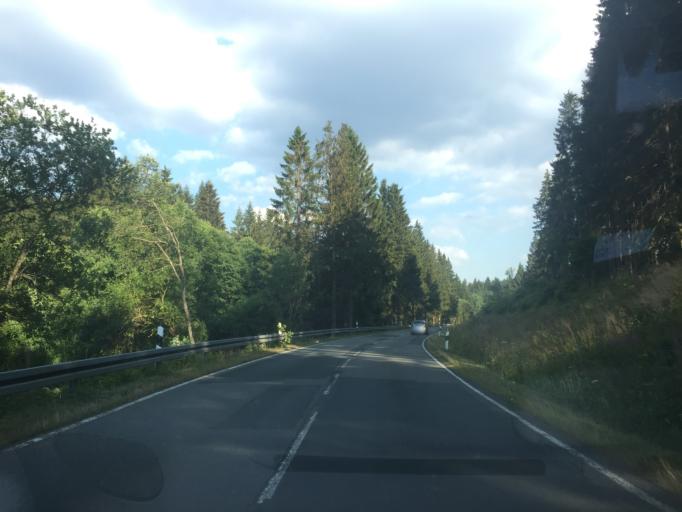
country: DE
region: Lower Saxony
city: Braunlage
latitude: 51.6993
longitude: 10.6225
